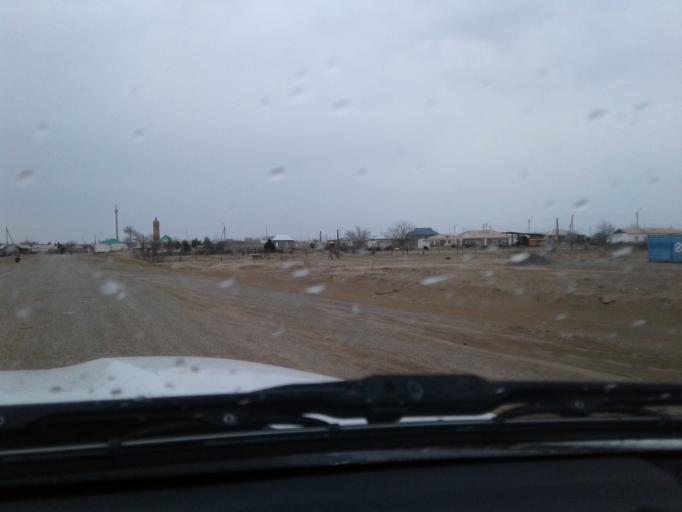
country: TM
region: Ahal
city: Abadan
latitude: 38.7587
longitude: 58.4916
